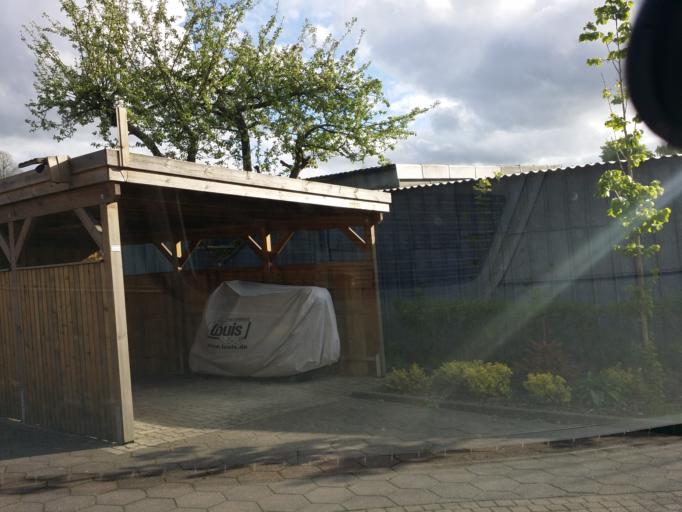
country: DE
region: Schleswig-Holstein
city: Kronshagen
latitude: 54.3443
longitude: 10.0965
